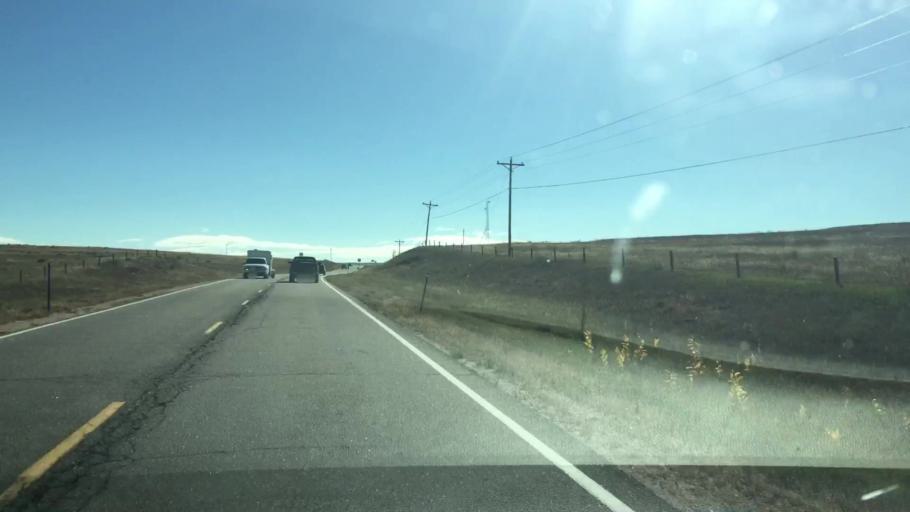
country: US
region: Colorado
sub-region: Elbert County
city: Kiowa
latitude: 39.3499
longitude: -104.4854
